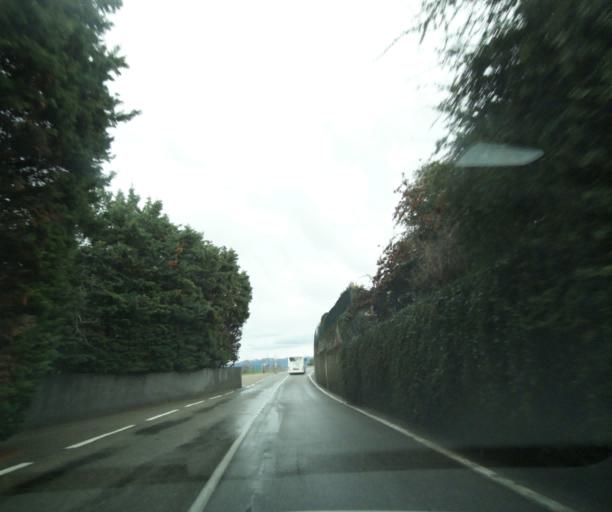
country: FR
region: Rhone-Alpes
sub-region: Departement de la Drome
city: Bourg-les-Valence
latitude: 44.9619
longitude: 4.8990
